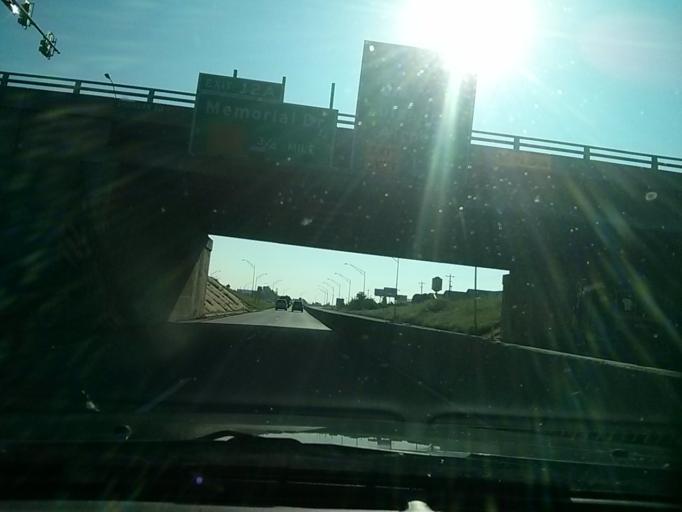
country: US
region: Oklahoma
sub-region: Tulsa County
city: Tulsa
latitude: 36.1629
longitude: -95.9049
